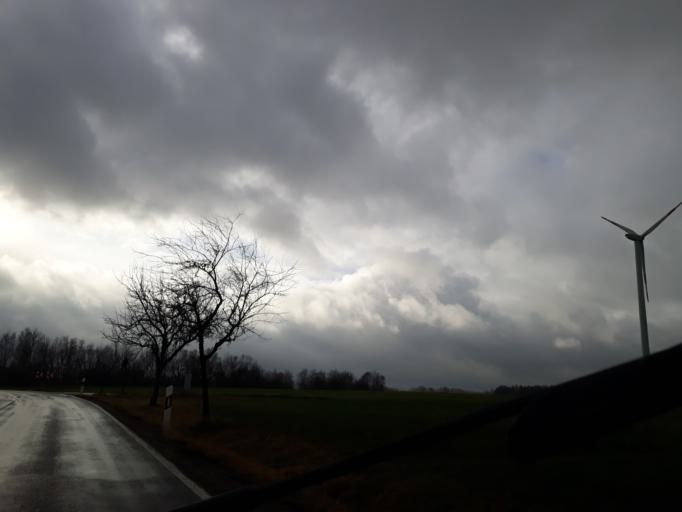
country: DE
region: Saxony
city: Herrnhut
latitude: 51.0094
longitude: 14.7279
